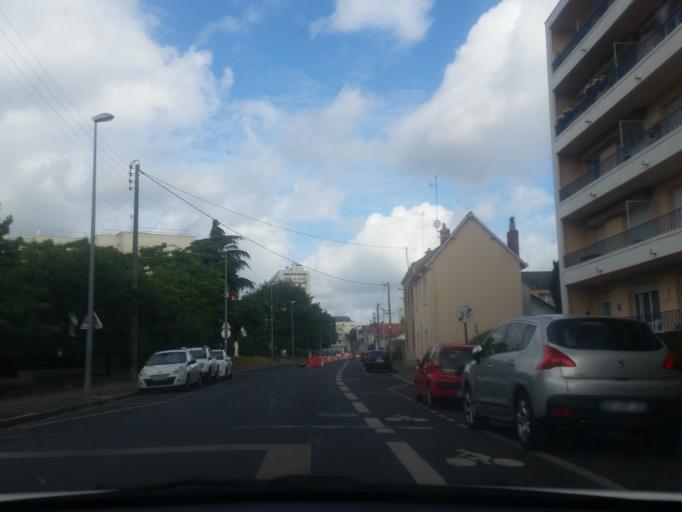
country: FR
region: Pays de la Loire
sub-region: Departement de la Loire-Atlantique
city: Nantes
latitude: 47.2387
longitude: -1.5271
